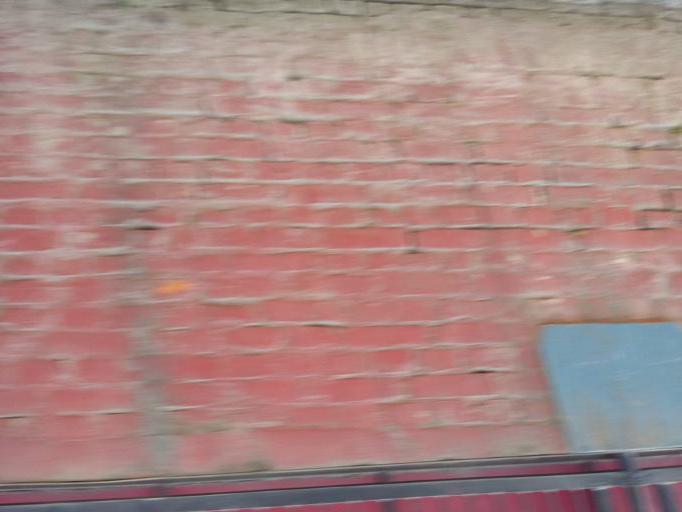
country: NP
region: Central Region
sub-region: Bagmati Zone
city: Kathmandu
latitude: 27.7229
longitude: 85.3356
